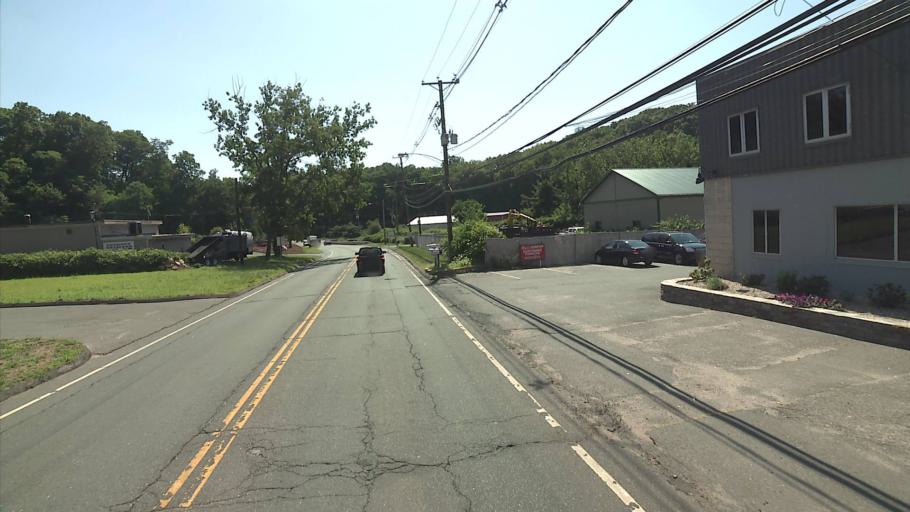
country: US
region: Connecticut
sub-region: Hartford County
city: Bristol
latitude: 41.6705
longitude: -72.9712
